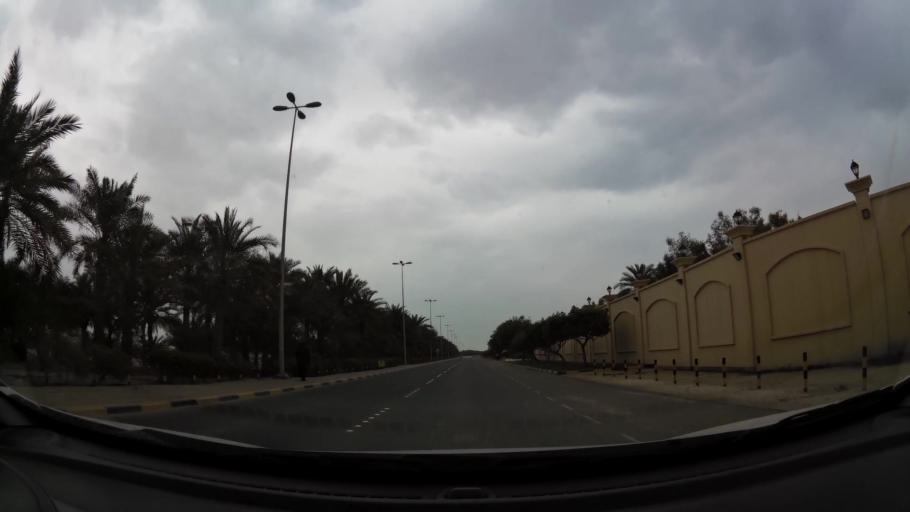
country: BH
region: Central Governorate
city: Dar Kulayb
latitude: 26.0455
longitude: 50.4885
